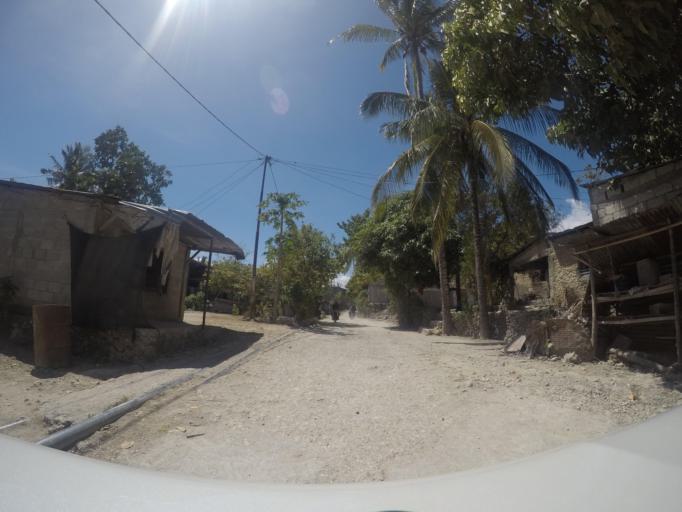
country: TL
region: Baucau
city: Baucau
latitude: -8.4670
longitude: 126.4581
